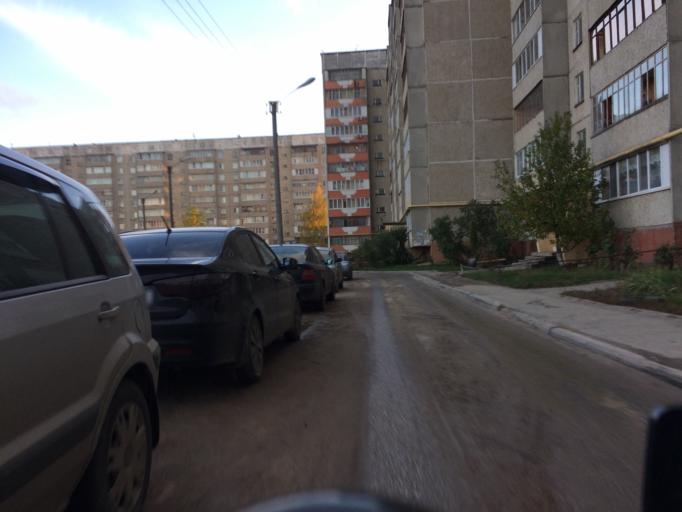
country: RU
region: Mariy-El
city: Yoshkar-Ola
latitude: 56.6362
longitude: 47.9279
